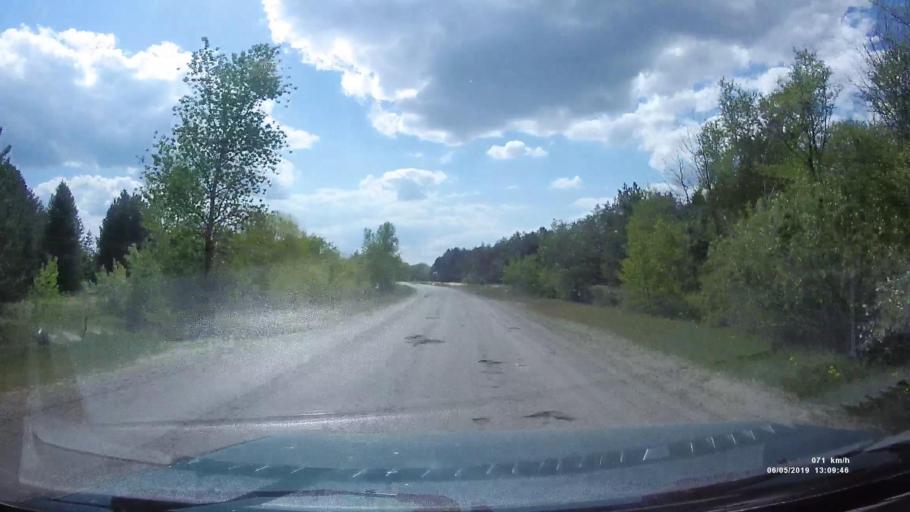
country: RU
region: Rostov
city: Ust'-Donetskiy
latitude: 47.7659
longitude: 40.9797
